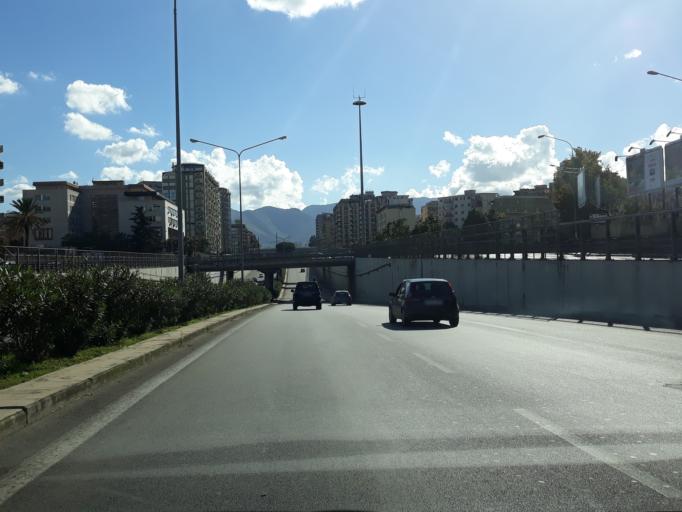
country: IT
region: Sicily
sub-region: Palermo
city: Palermo
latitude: 38.1308
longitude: 13.3299
